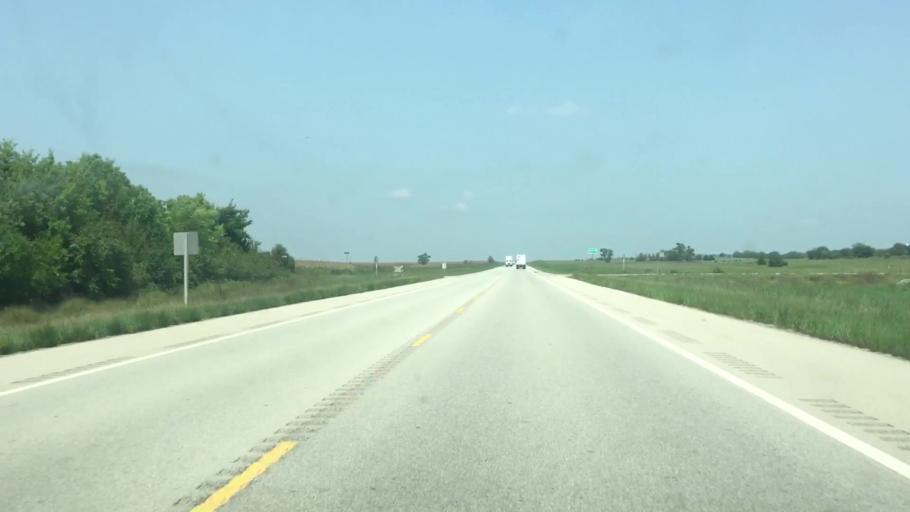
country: US
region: Kansas
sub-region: Allen County
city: Iola
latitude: 38.0376
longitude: -95.3805
